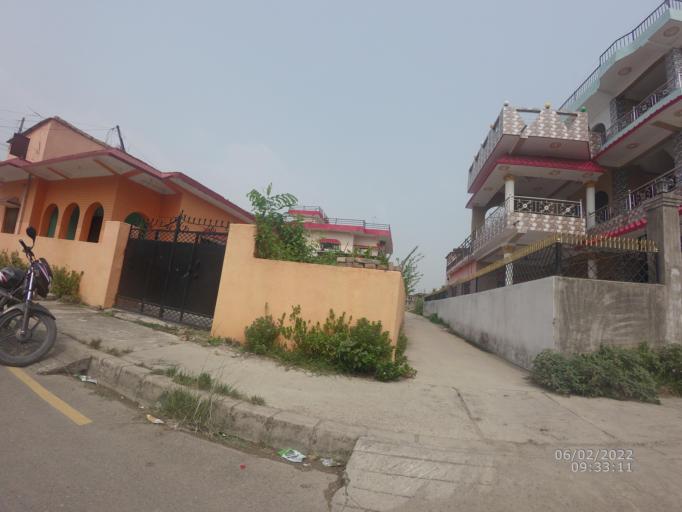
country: NP
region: Western Region
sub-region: Lumbini Zone
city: Bhairahawa
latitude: 27.4984
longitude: 83.4534
